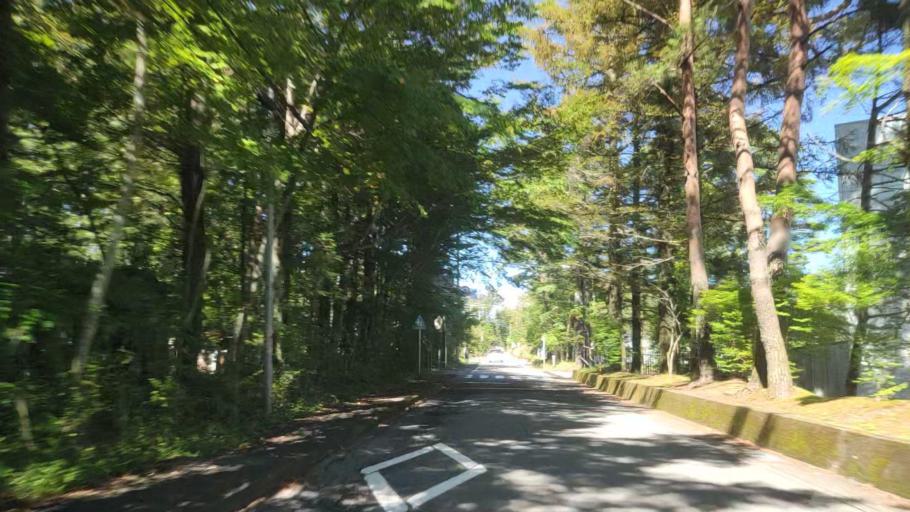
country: JP
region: Shizuoka
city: Gotemba
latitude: 35.4088
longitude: 138.8566
